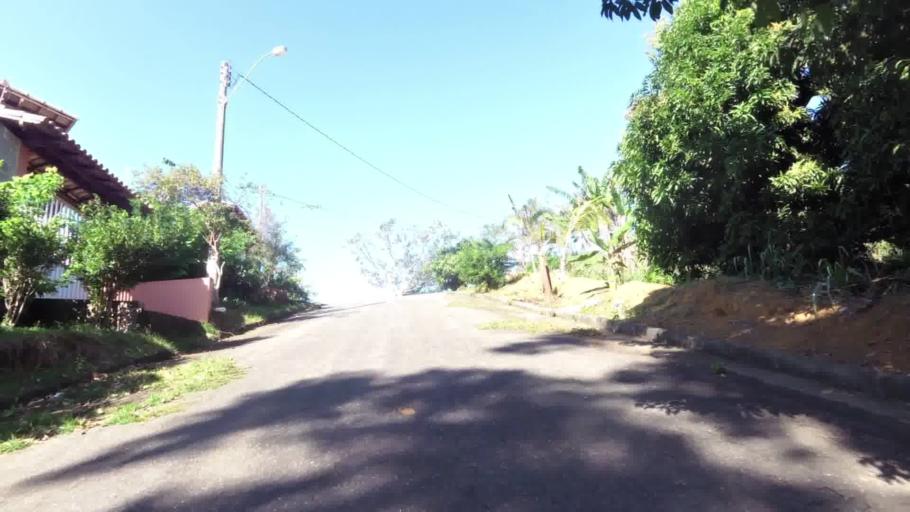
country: BR
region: Espirito Santo
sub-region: Guarapari
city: Guarapari
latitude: -20.7383
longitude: -40.5575
